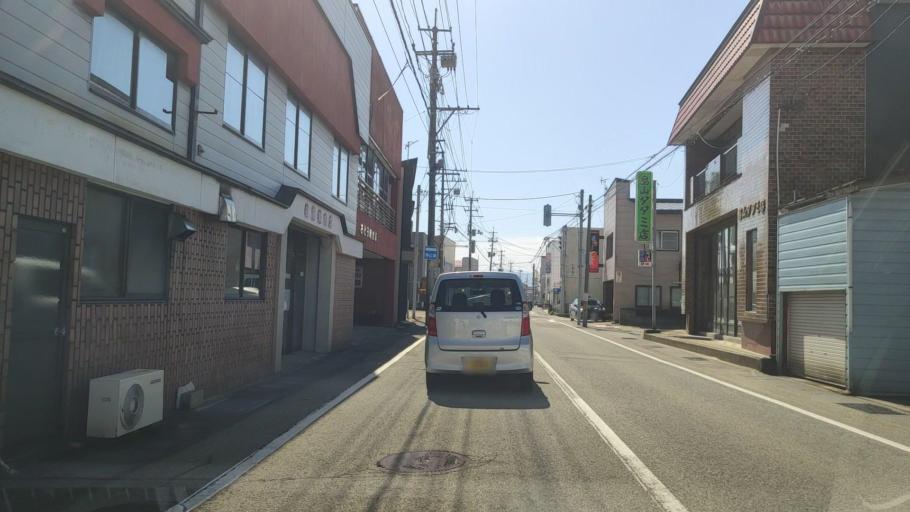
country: JP
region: Akita
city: Omagari
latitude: 39.4692
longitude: 140.4741
